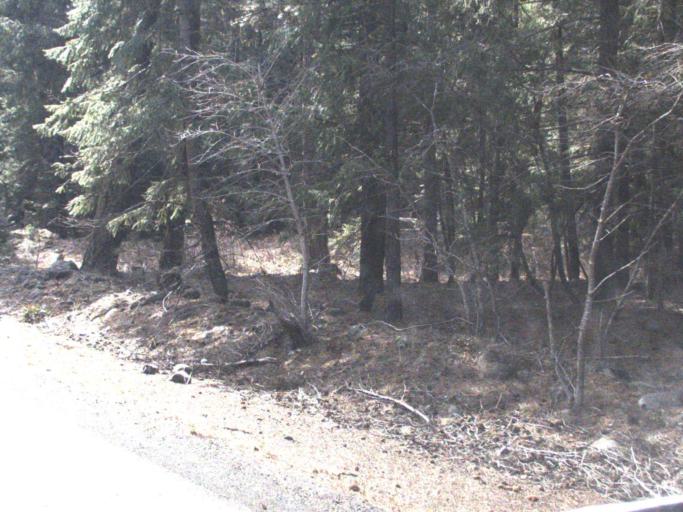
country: US
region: Washington
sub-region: Kittitas County
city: Cle Elum
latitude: 46.9770
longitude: -121.0946
